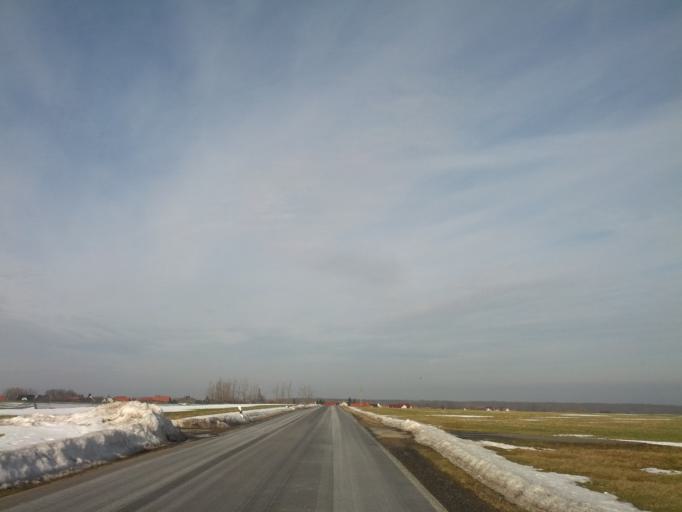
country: DE
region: Thuringia
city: Weberstedt
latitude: 51.0563
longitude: 10.4943
